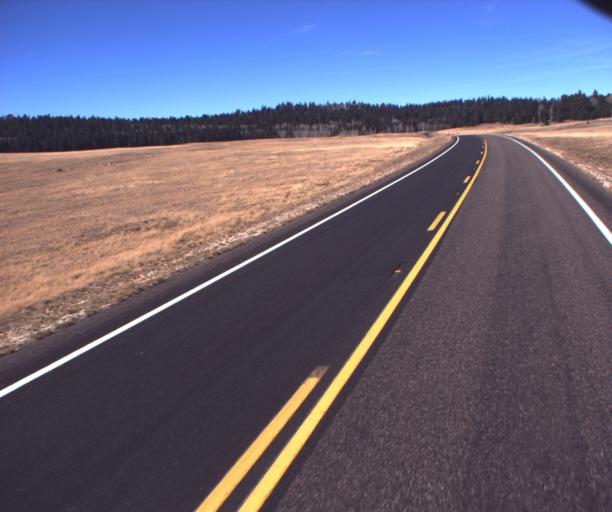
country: US
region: Arizona
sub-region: Coconino County
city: Grand Canyon
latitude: 36.4978
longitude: -112.1337
